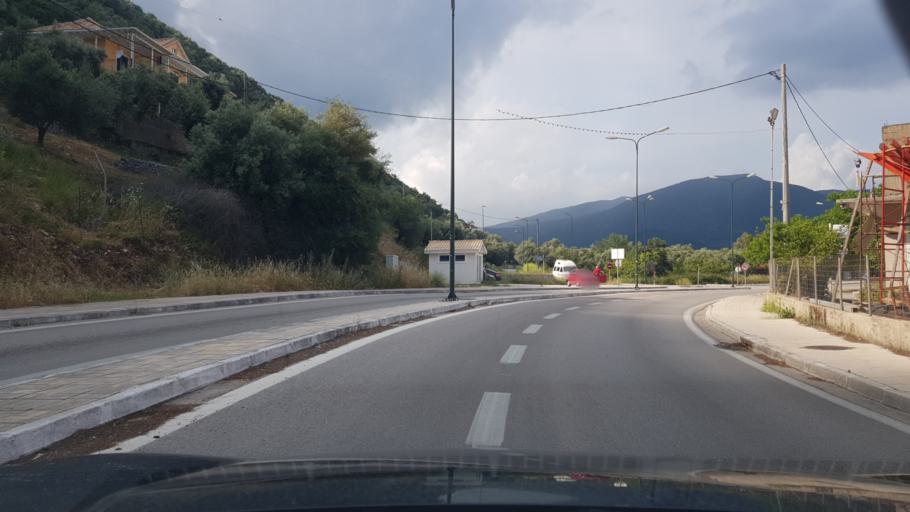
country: GR
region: Ionian Islands
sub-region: Lefkada
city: Nidri
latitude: 38.6906
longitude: 20.6983
